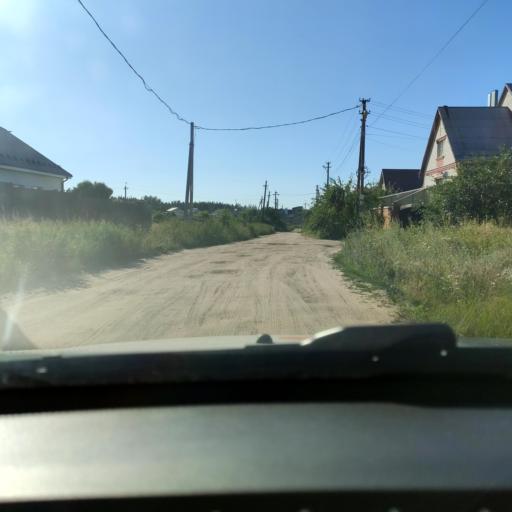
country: RU
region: Voronezj
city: Pridonskoy
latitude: 51.6302
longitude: 39.0907
